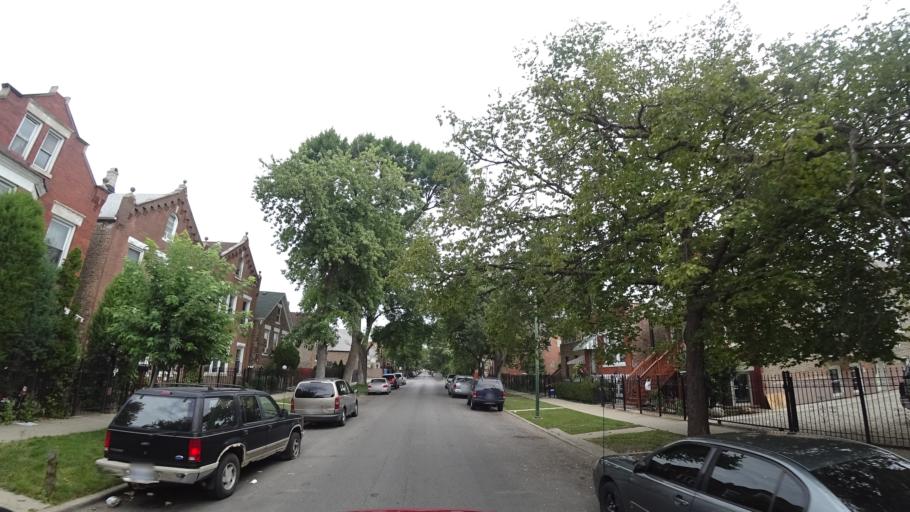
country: US
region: Illinois
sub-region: Cook County
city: Cicero
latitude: 41.8401
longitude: -87.7122
